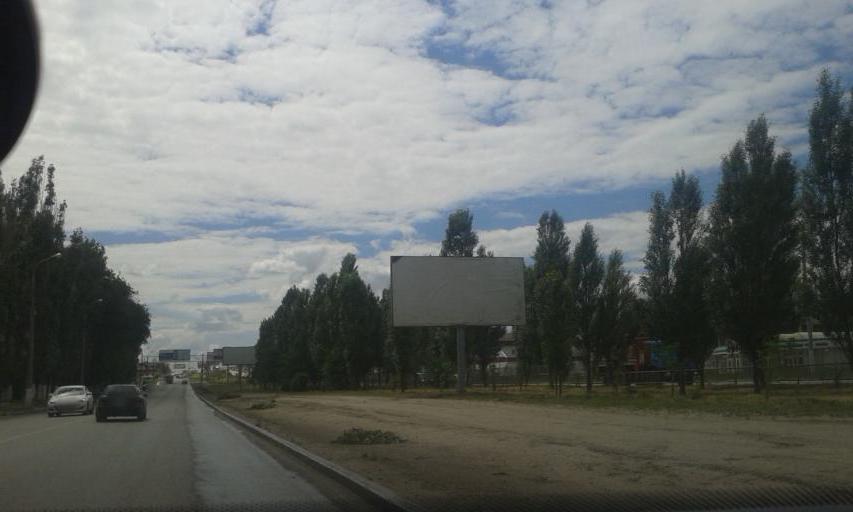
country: RU
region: Volgograd
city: Volgograd
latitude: 48.7578
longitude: 44.4961
